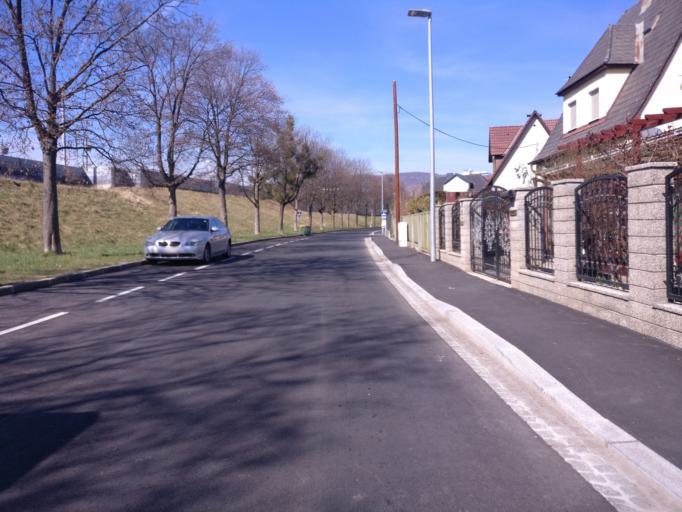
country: AT
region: Styria
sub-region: Graz Stadt
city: Wetzelsdorf
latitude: 47.0568
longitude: 15.4217
